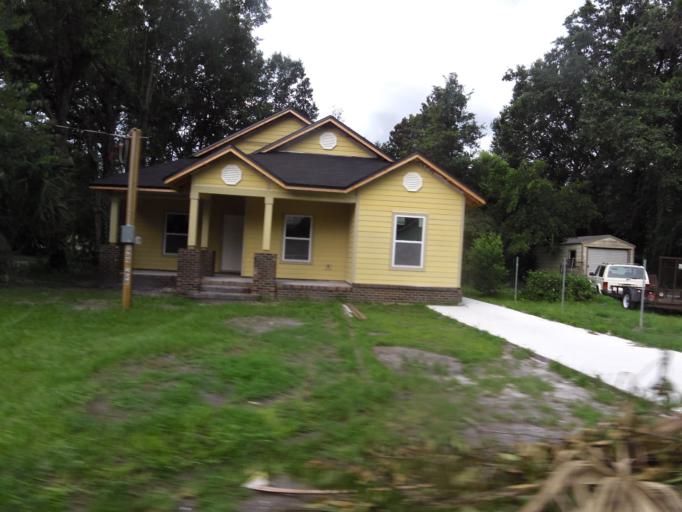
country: US
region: Florida
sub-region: Duval County
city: Jacksonville
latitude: 30.3523
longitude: -81.6350
